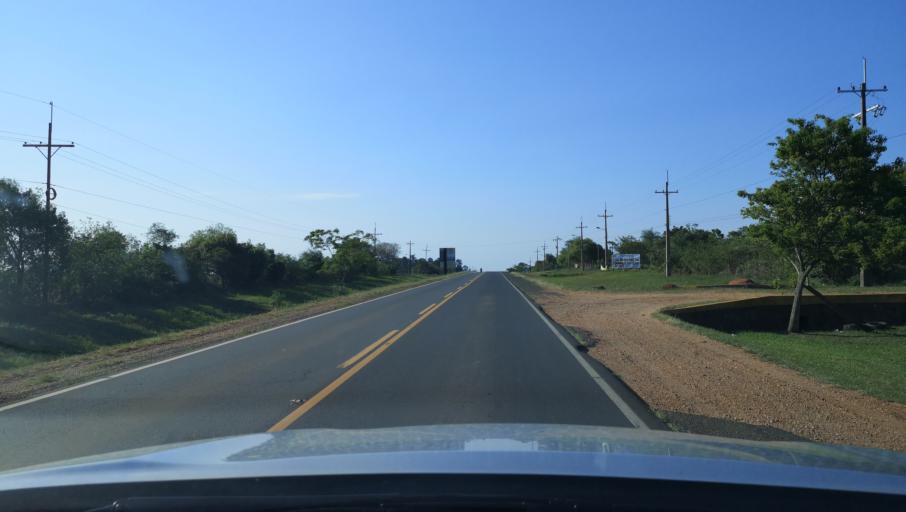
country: PY
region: Misiones
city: Santa Maria
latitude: -26.8551
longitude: -57.0355
